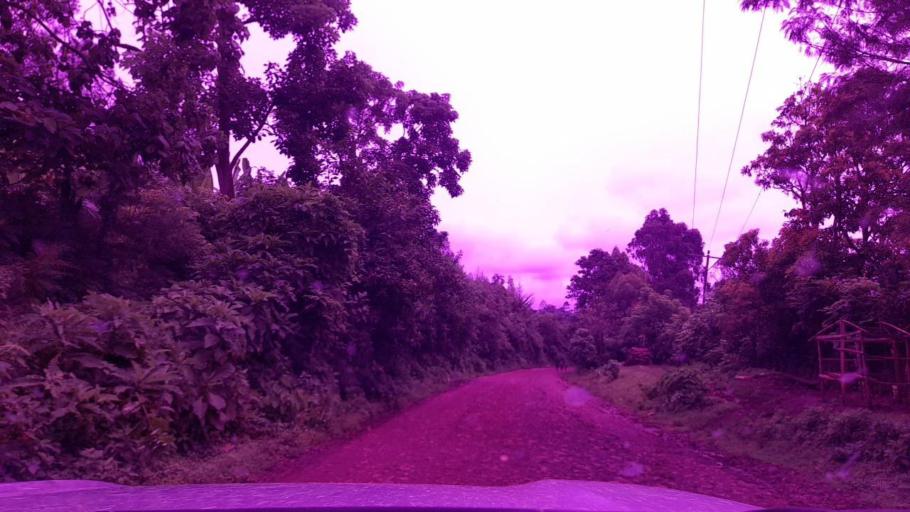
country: ET
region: Southern Nations, Nationalities, and People's Region
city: Tippi
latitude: 7.5848
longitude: 35.7708
